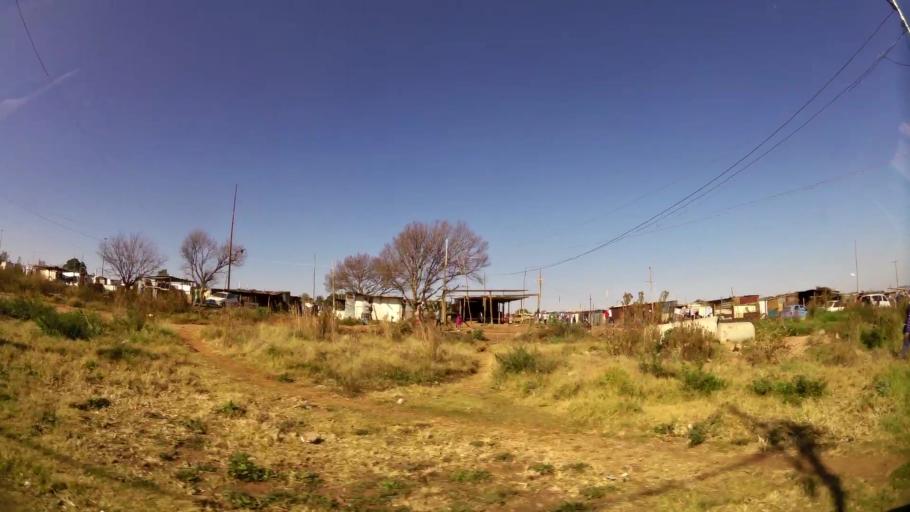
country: ZA
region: Gauteng
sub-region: City of Johannesburg Metropolitan Municipality
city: Johannesburg
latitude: -26.1929
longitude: 27.9779
